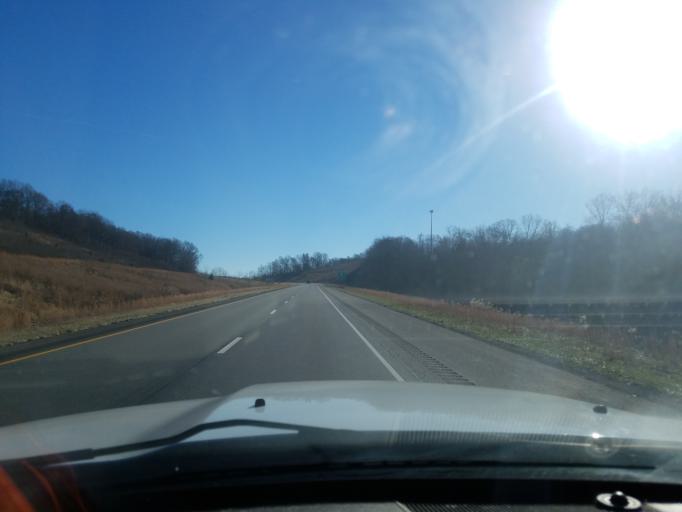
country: US
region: Indiana
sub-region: Crawford County
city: English
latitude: 38.2313
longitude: -86.6196
